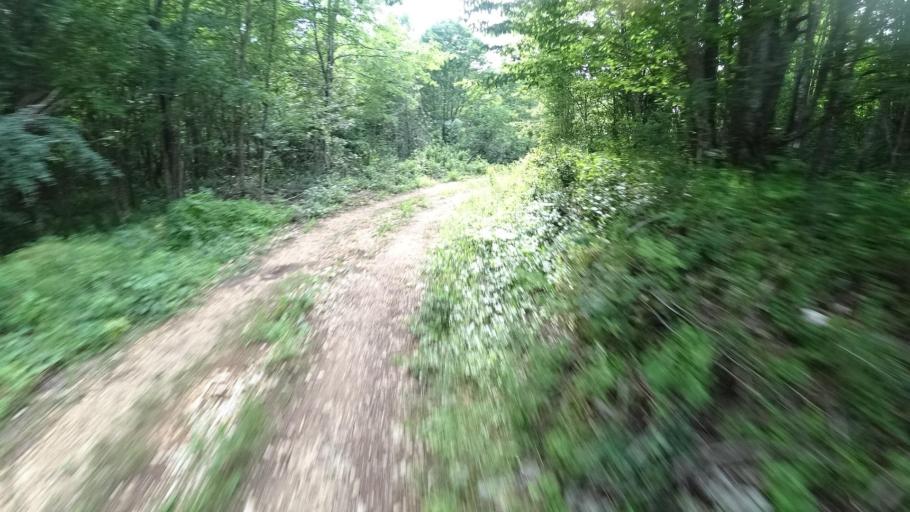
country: HR
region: Licko-Senjska
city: Jezerce
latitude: 44.9027
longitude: 15.6533
